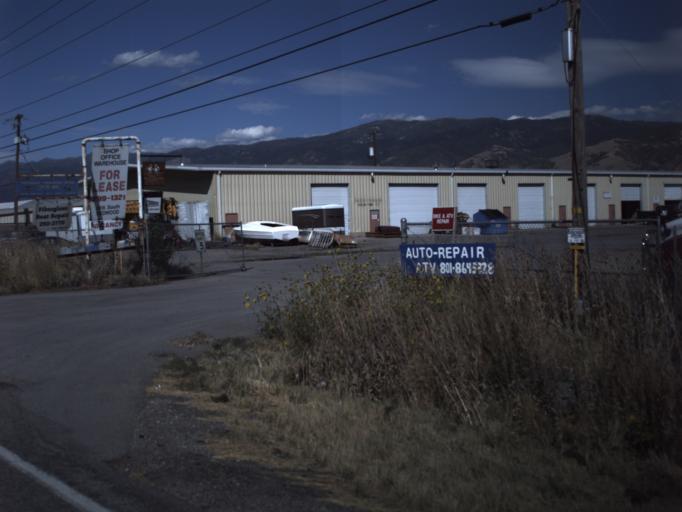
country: US
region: Utah
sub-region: Davis County
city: North Salt Lake
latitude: 40.8644
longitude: -111.9299
